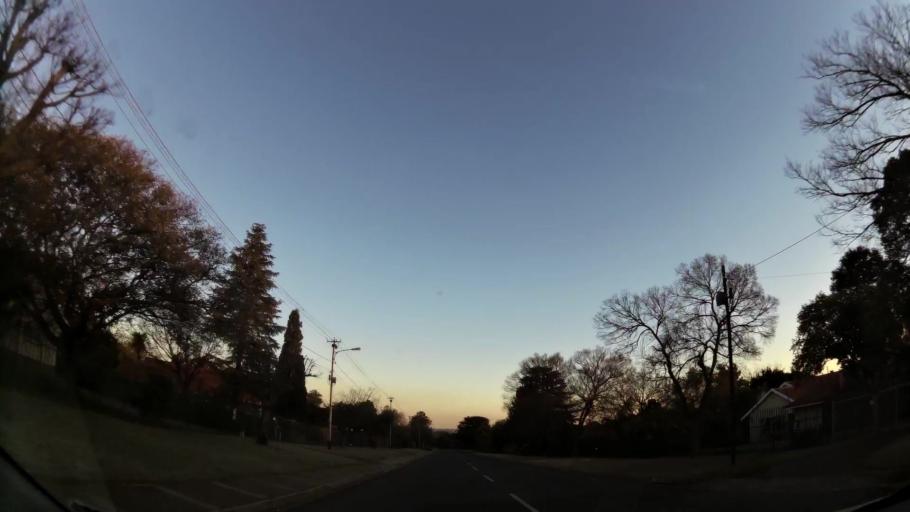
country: ZA
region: Gauteng
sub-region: City of Johannesburg Metropolitan Municipality
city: Roodepoort
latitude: -26.1558
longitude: 27.9081
